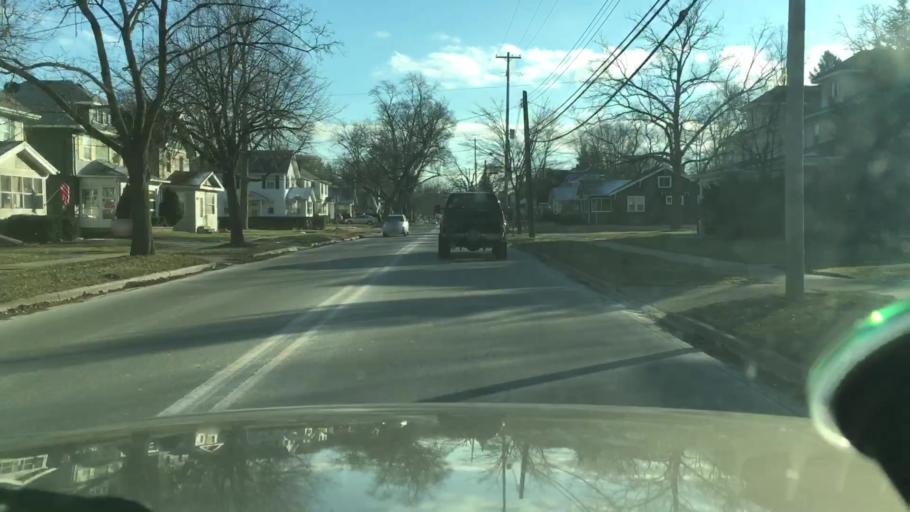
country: US
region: Michigan
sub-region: Jackson County
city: Jackson
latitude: 42.2390
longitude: -84.4234
